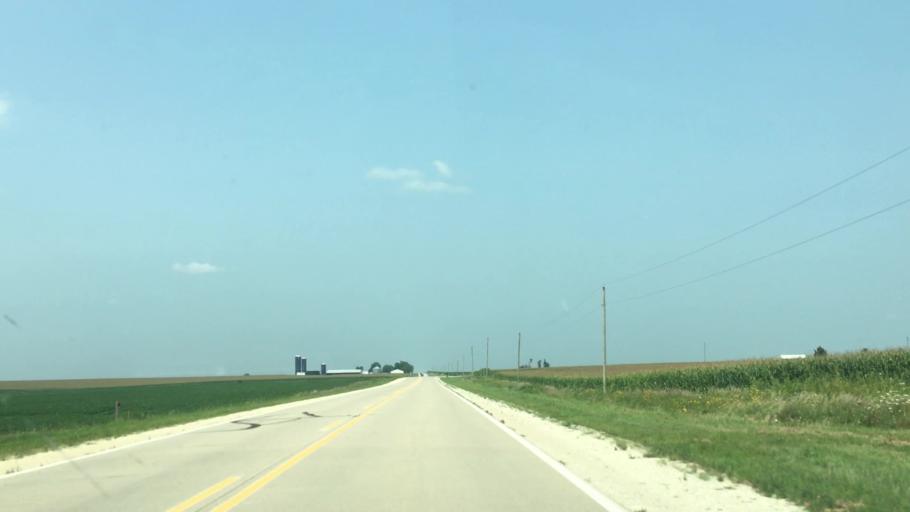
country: US
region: Iowa
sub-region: Fayette County
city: Fayette
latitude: 42.7331
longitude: -91.8041
